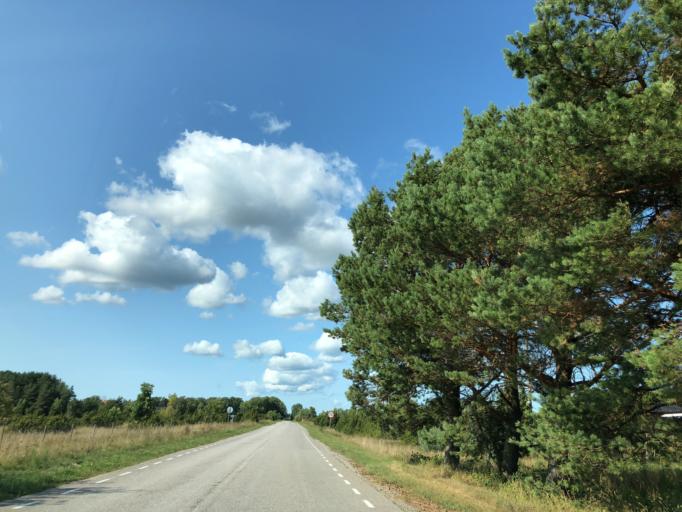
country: EE
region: Hiiumaa
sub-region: Kaerdla linn
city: Kardla
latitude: 58.7916
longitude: 22.7699
